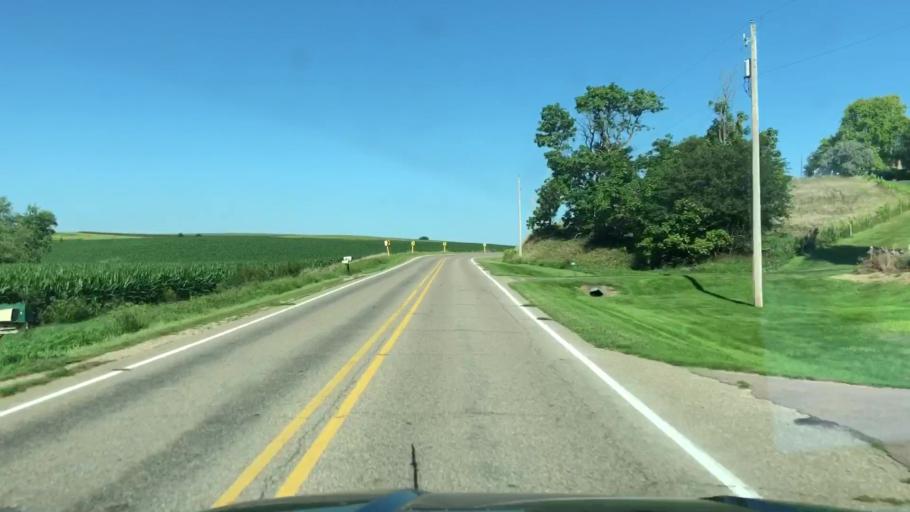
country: US
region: Iowa
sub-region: Woodbury County
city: Sergeant Bluff
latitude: 42.4215
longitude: -96.2723
